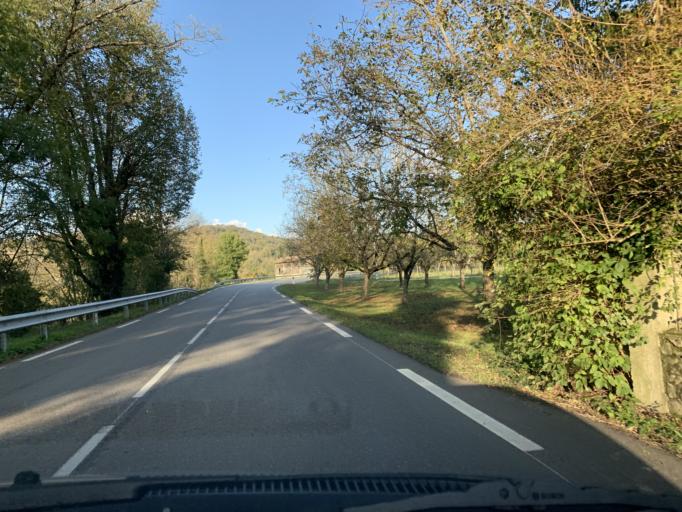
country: FR
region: Rhone-Alpes
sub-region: Departement de l'Isere
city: Saint-Just-de-Claix
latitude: 45.0543
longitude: 5.2772
